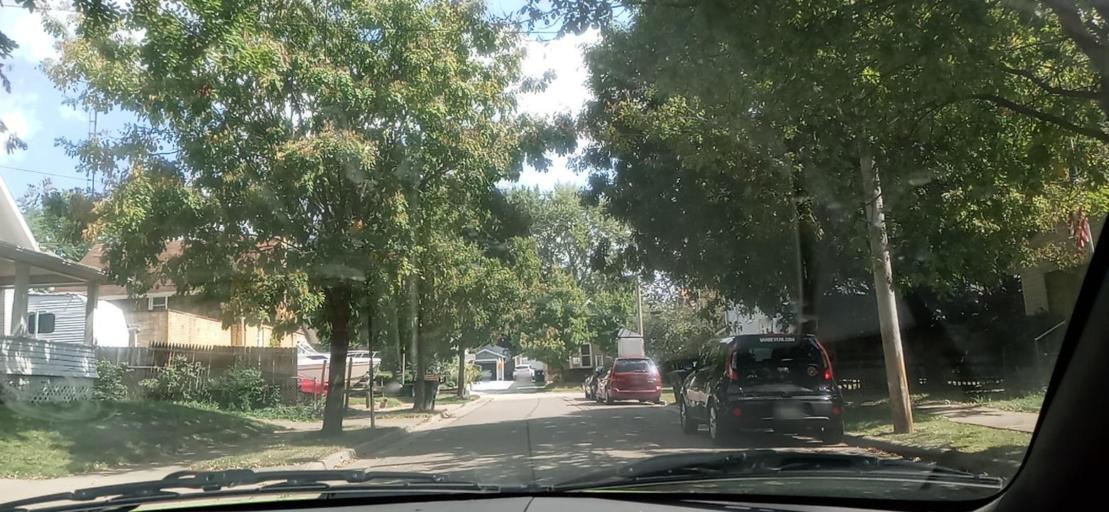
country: US
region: Ohio
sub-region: Summit County
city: Portage Lakes
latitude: 41.0407
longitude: -81.5591
